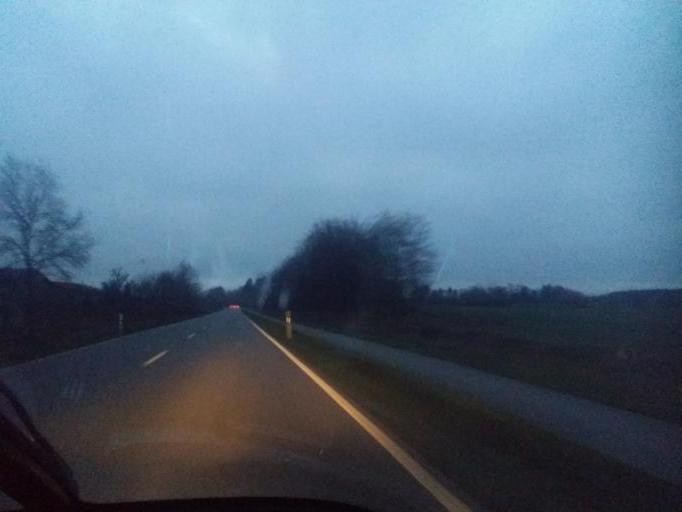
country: DE
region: Schleswig-Holstein
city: Poschendorf
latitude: 54.0289
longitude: 9.4771
